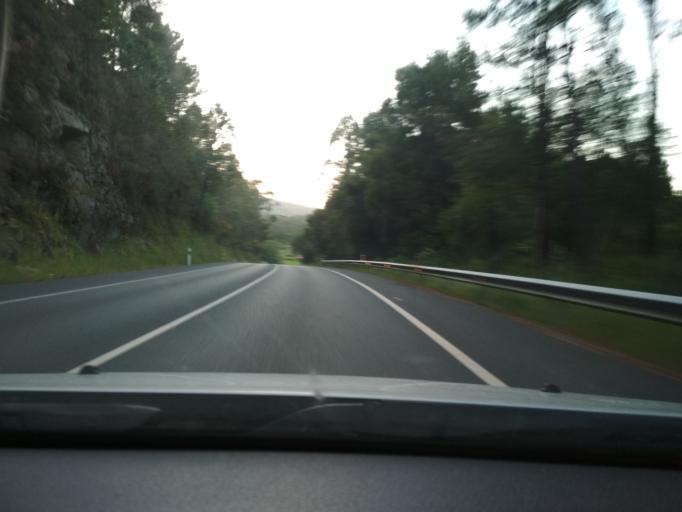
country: ES
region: Galicia
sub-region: Provincia de Pontevedra
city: Caldas de Reis
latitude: 42.6381
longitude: -8.6488
